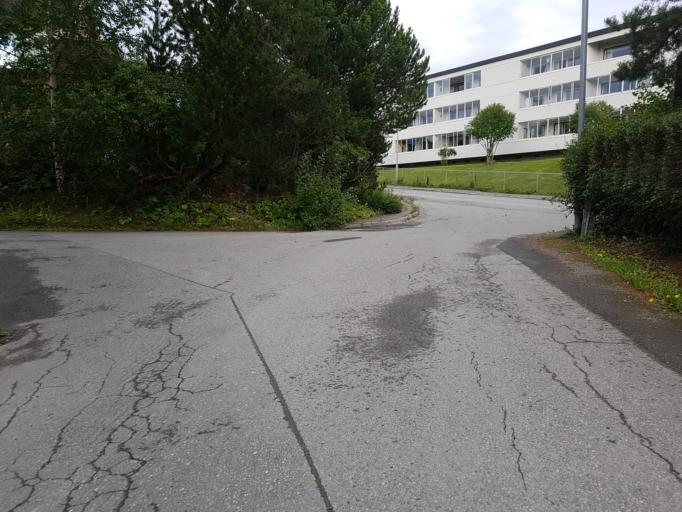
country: NO
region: Sor-Trondelag
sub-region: Trondheim
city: Trondheim
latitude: 63.4027
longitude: 10.4141
